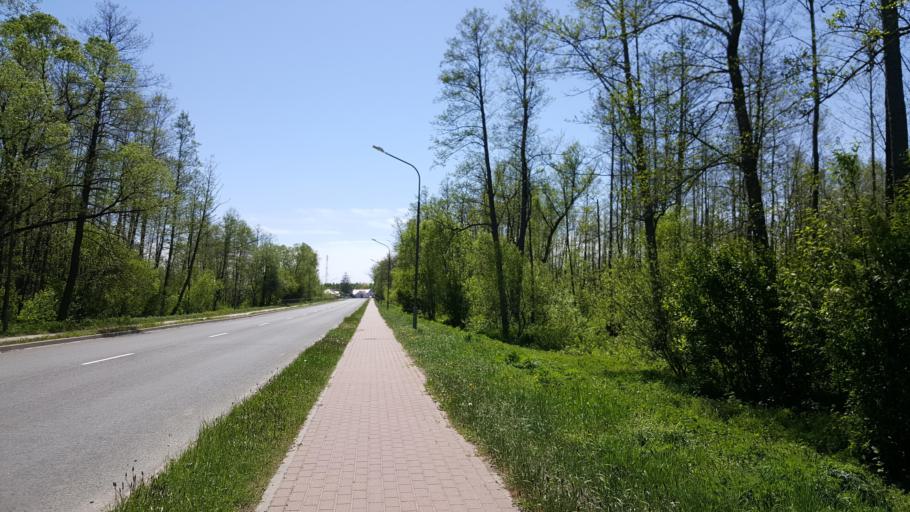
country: BY
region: Brest
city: Kamyanyuki
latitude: 52.5671
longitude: 23.8019
